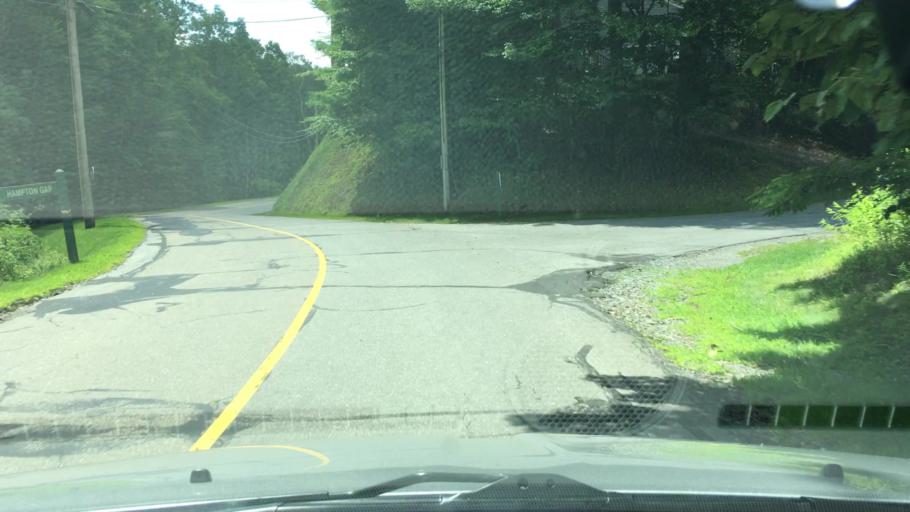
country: US
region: North Carolina
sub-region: Madison County
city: Mars Hill
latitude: 35.9699
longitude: -82.5058
